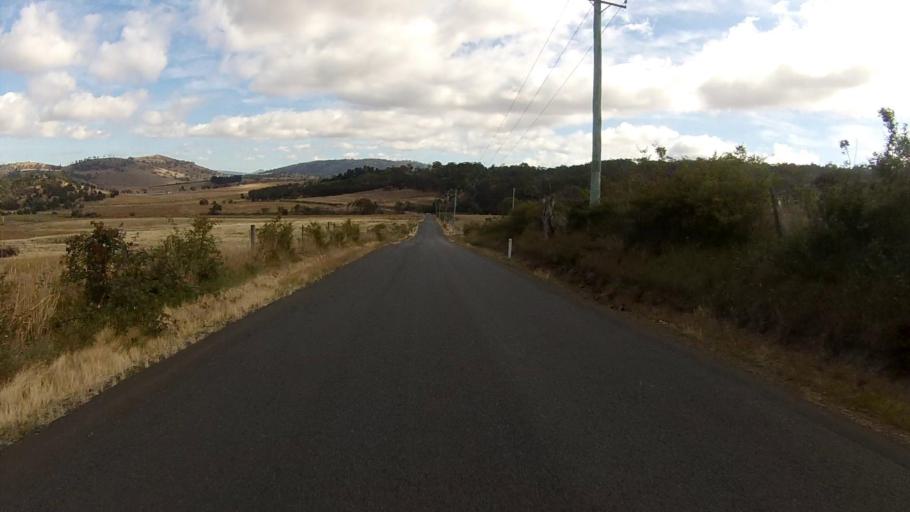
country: AU
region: Tasmania
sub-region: Brighton
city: Old Beach
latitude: -42.7566
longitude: 147.3048
